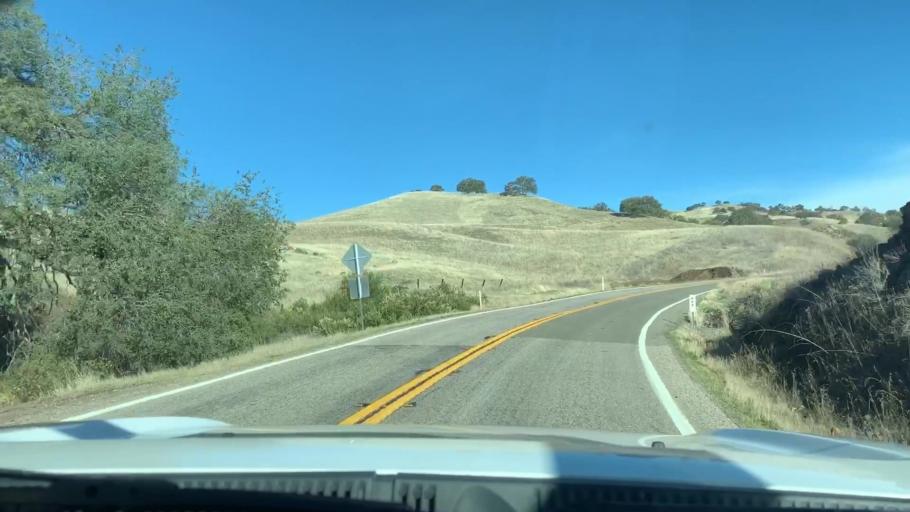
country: US
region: California
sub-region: Monterey County
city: King City
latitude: 36.1927
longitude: -120.7997
